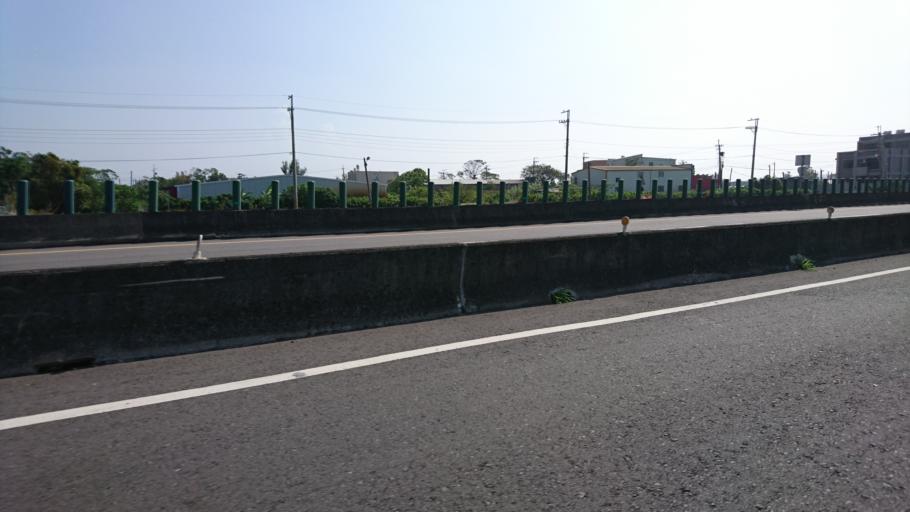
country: TW
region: Taiwan
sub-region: Miaoli
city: Miaoli
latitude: 24.6884
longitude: 120.8542
